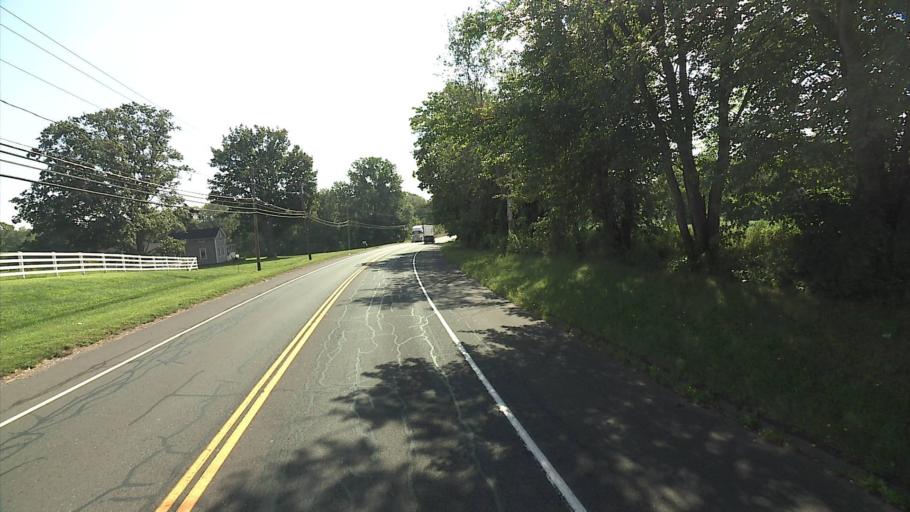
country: US
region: Connecticut
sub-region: Tolland County
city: Somers
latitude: 41.9871
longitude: -72.4758
